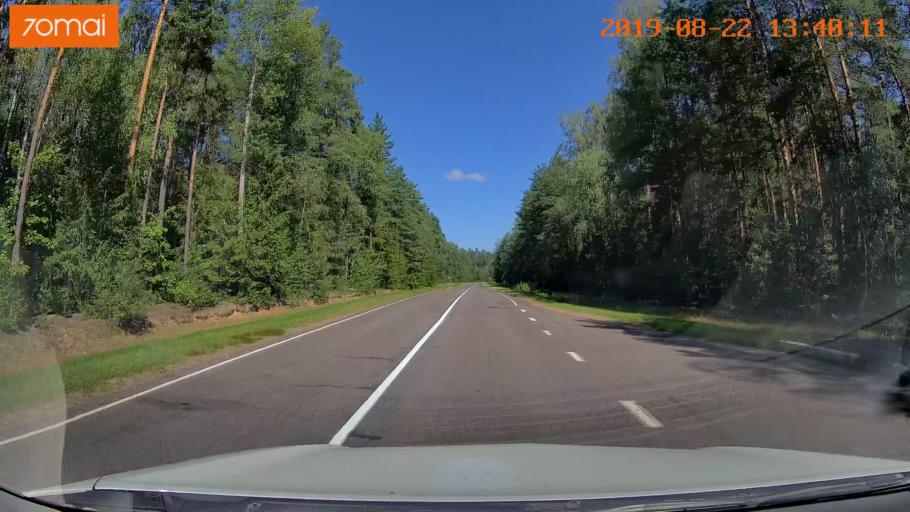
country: BY
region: Minsk
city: Staryya Darohi
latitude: 53.2344
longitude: 28.3626
